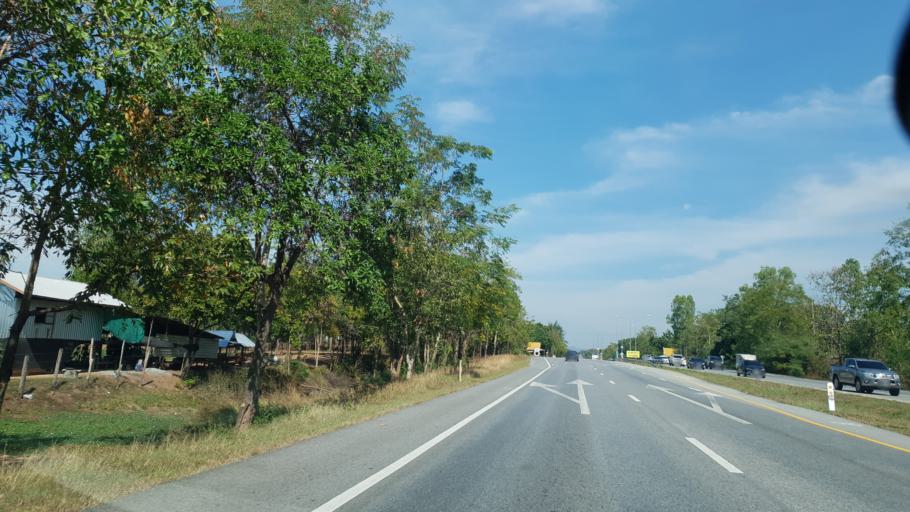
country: TH
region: Uttaradit
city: Thong Saen Khan
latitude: 17.4318
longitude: 100.2277
